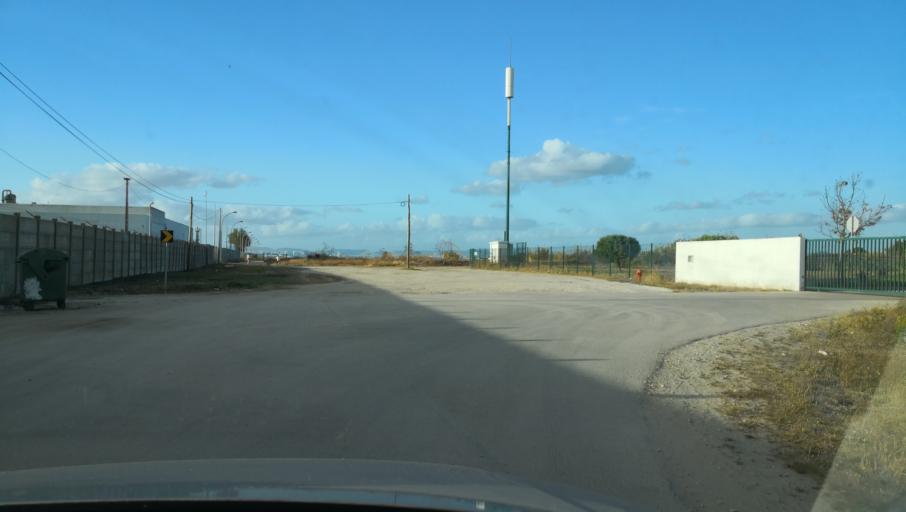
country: PT
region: Setubal
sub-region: Barreiro
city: Barreiro
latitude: 38.6750
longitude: -9.0466
